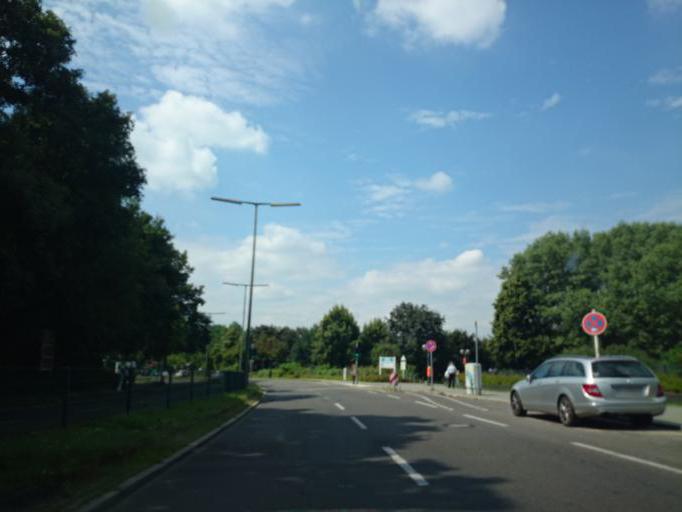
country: DE
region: Berlin
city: Wannsee
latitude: 52.4212
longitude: 13.1771
